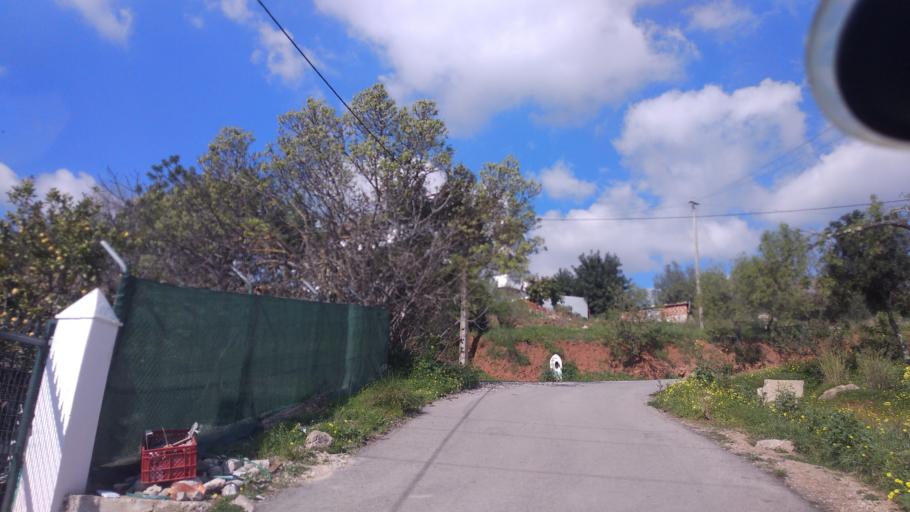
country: PT
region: Faro
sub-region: Sao Bras de Alportel
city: Sao Bras de Alportel
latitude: 37.1494
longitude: -7.8856
